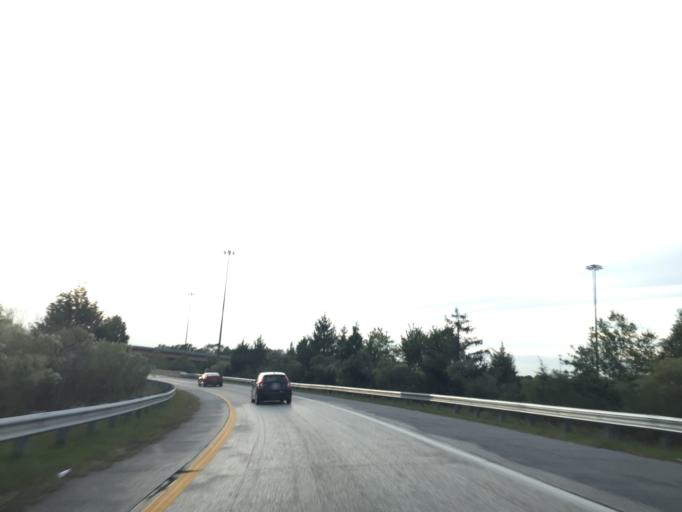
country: US
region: Maryland
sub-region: Prince George's County
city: Glenarden
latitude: 38.9473
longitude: -76.8573
